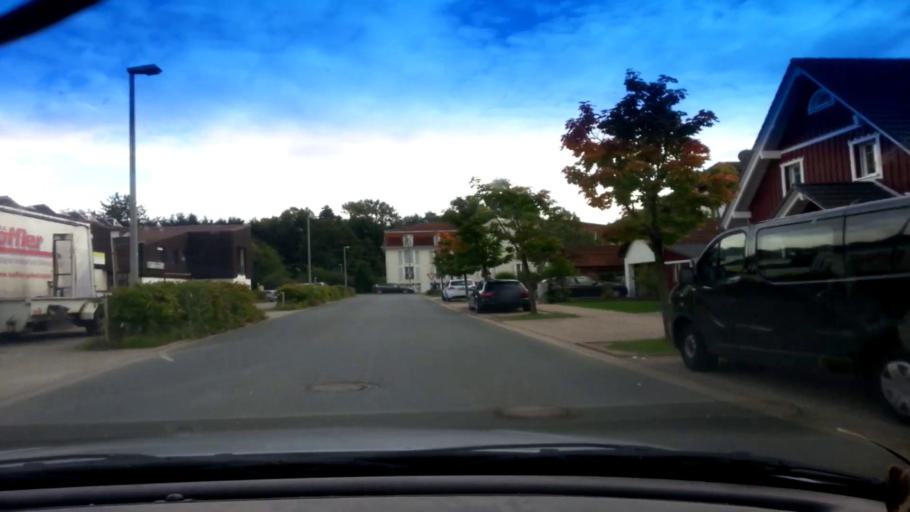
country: DE
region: Bavaria
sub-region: Upper Franconia
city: Kemmern
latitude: 49.9564
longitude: 10.8820
